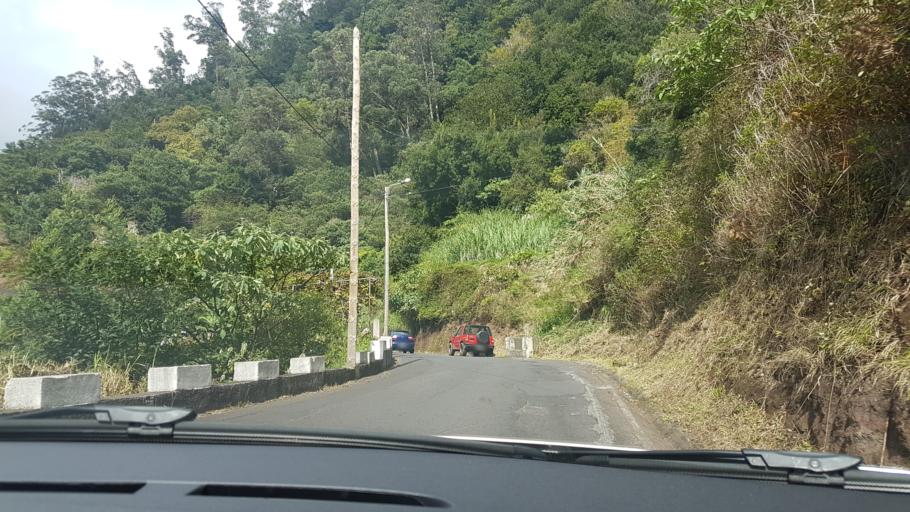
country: PT
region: Madeira
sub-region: Santa Cruz
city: Santa Cruz
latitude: 32.7358
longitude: -16.8069
